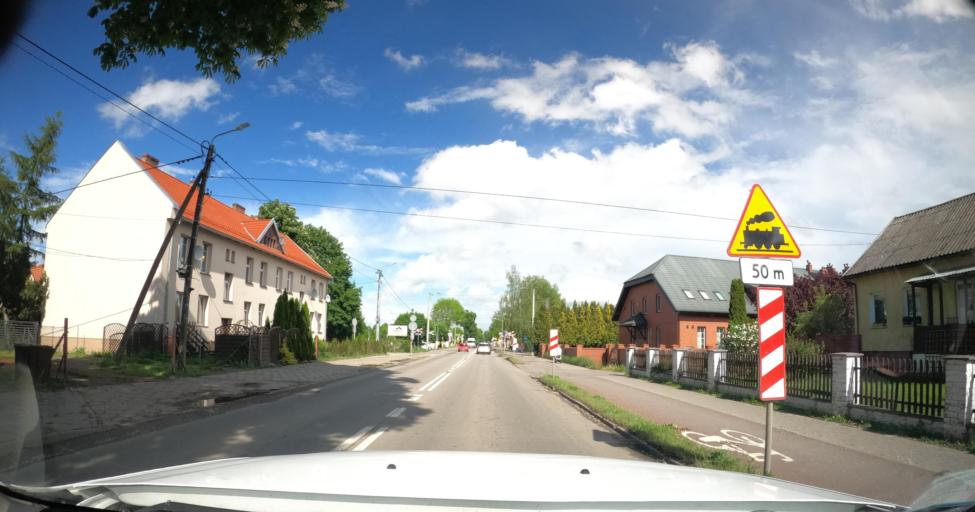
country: PL
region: Pomeranian Voivodeship
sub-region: Powiat nowodworski
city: Nowy Dwor Gdanski
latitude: 54.2084
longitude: 19.1220
